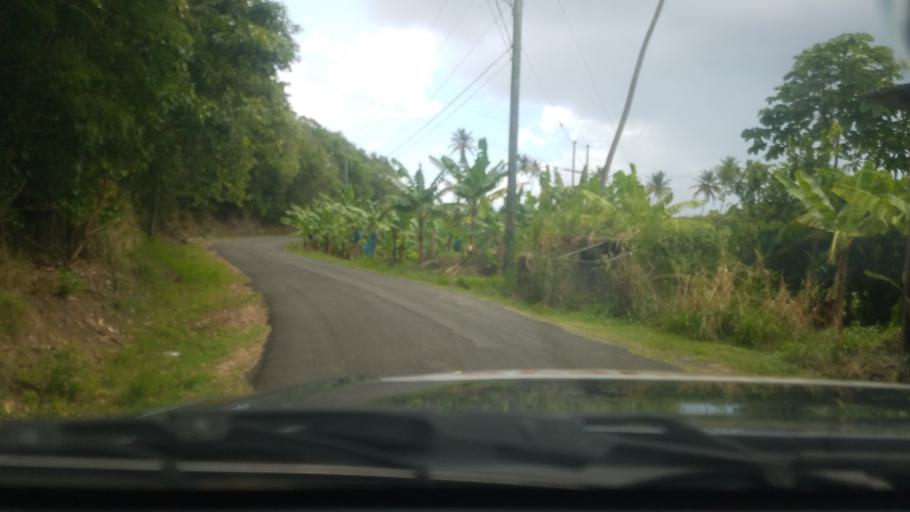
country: LC
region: Praslin
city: Praslin
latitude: 13.8699
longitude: -60.9007
